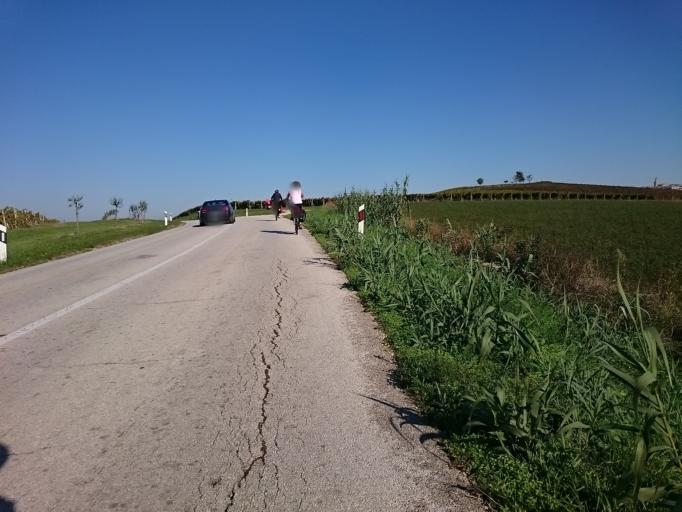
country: HR
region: Istarska
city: Buje
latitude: 45.3967
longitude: 13.6409
